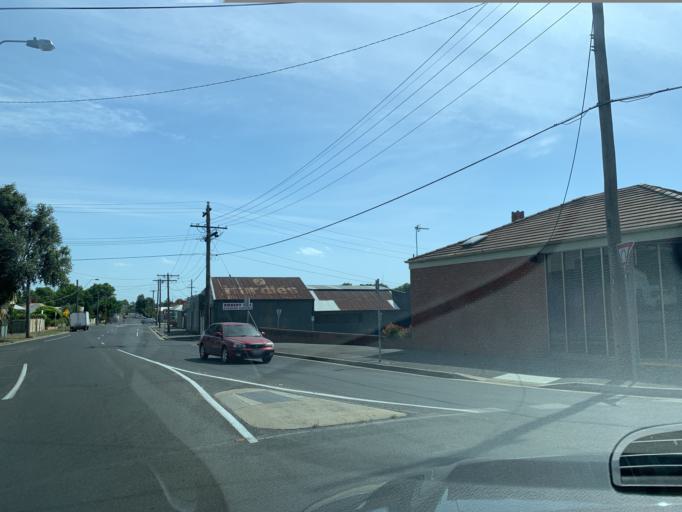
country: AU
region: Victoria
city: Ballarat East
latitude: -37.5640
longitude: 143.8657
